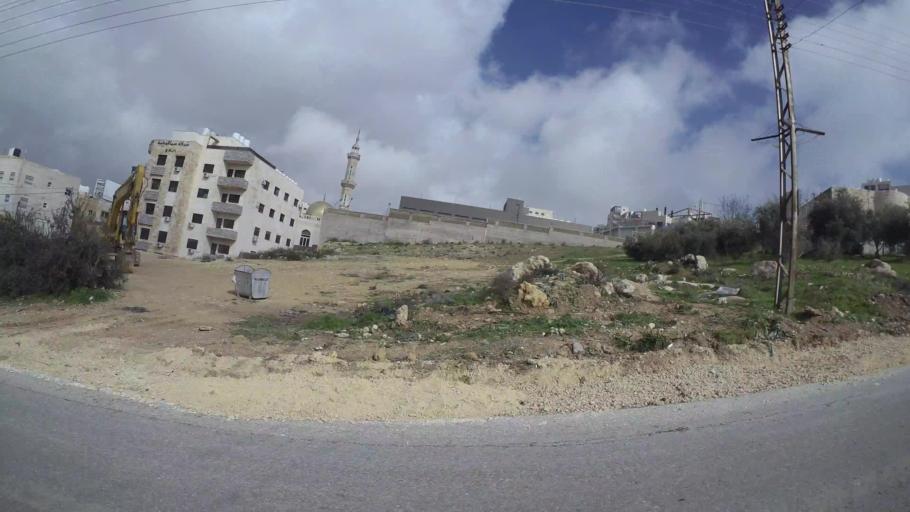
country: JO
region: Amman
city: Al Jubayhah
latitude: 32.0619
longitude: 35.8683
